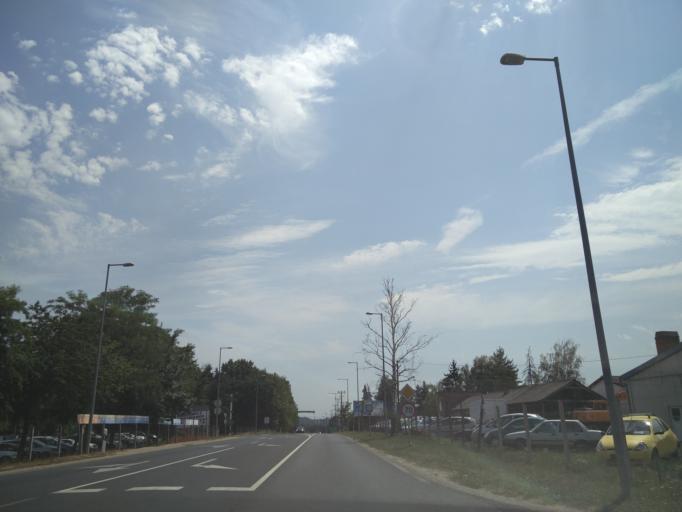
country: HU
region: Zala
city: Zalaegerszeg
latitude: 46.8670
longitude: 16.8536
